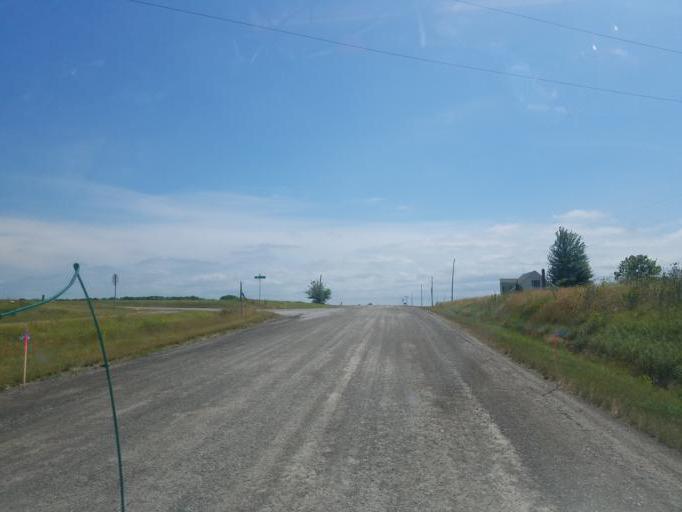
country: US
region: Indiana
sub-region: Allen County
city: Woodburn
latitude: 41.1644
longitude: -84.8490
